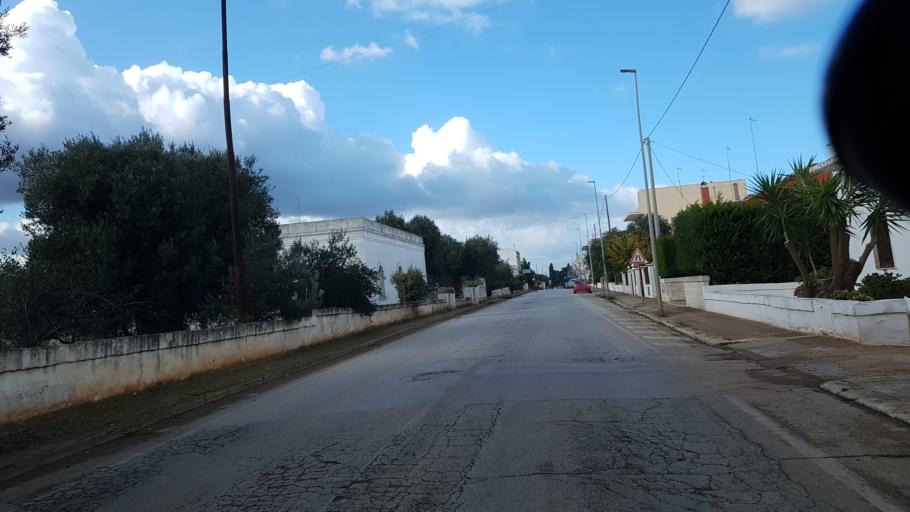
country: IT
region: Apulia
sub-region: Provincia di Brindisi
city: Montalbano
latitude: 40.7904
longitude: 17.4627
